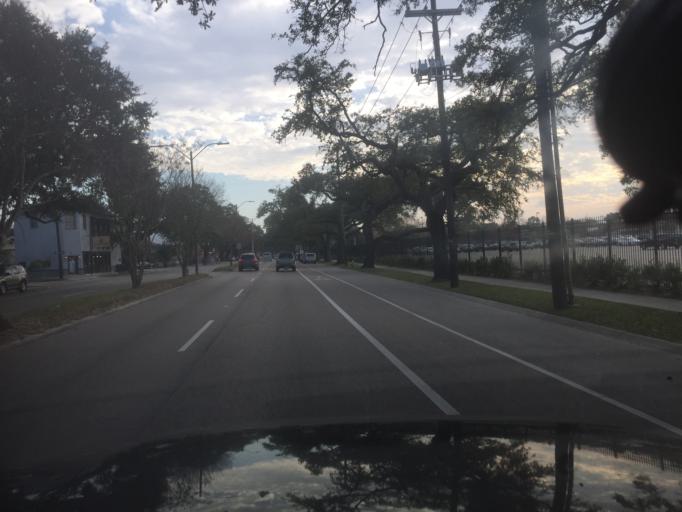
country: US
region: Louisiana
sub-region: Orleans Parish
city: New Orleans
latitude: 29.9835
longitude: -90.0769
